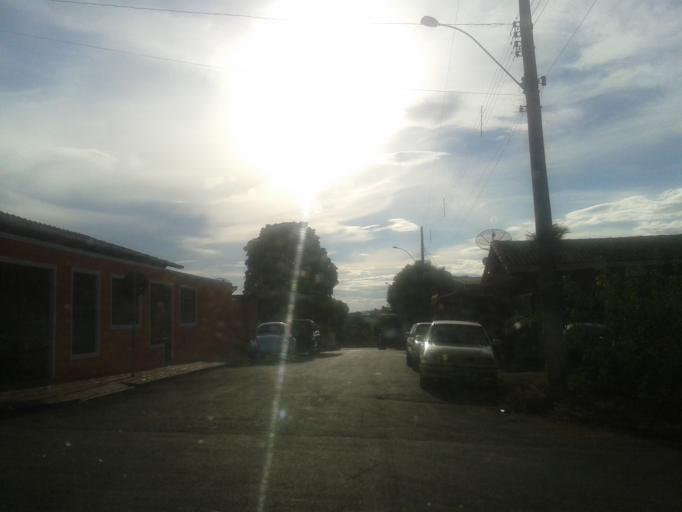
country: BR
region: Minas Gerais
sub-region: Capinopolis
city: Capinopolis
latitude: -18.6789
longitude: -49.5673
